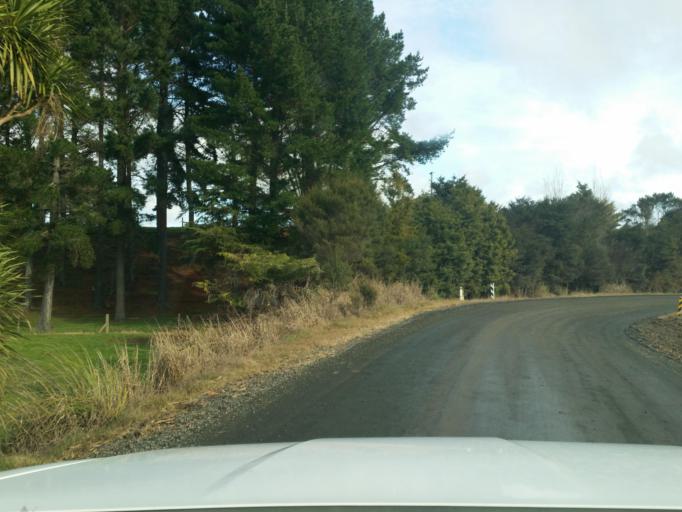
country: NZ
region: Northland
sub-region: Kaipara District
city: Dargaville
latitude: -35.8149
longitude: 173.7579
